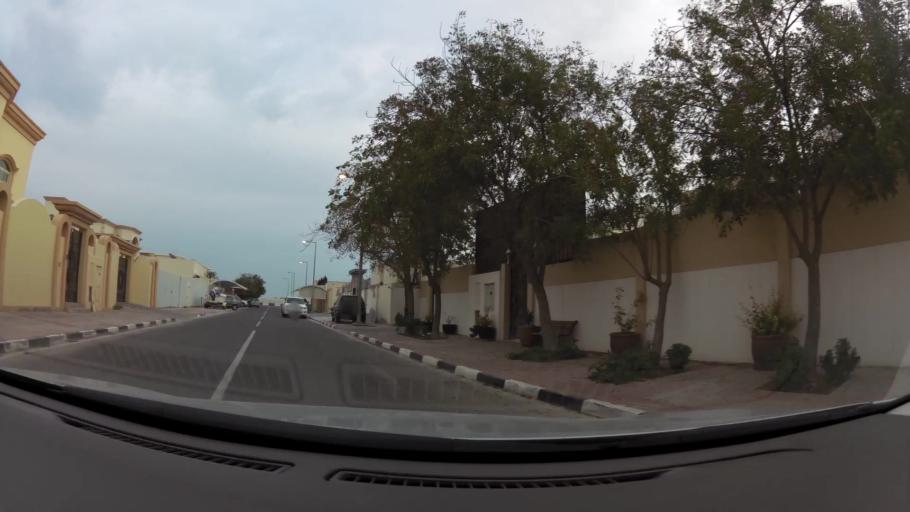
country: QA
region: Baladiyat ad Dawhah
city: Doha
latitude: 25.3381
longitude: 51.5093
